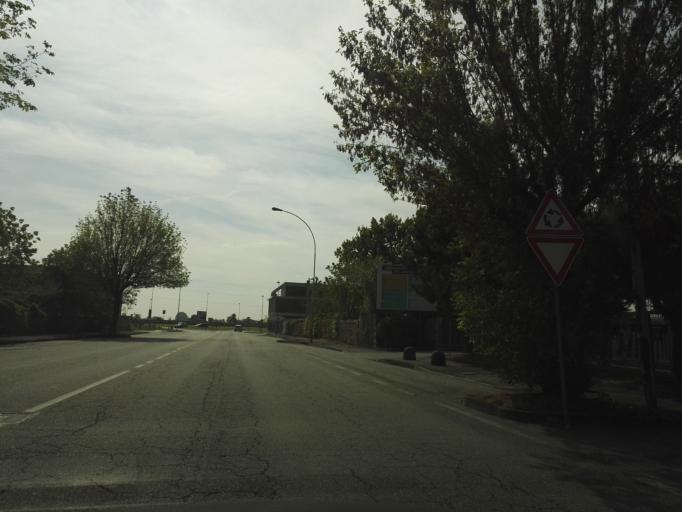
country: IT
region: Lombardy
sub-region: Citta metropolitana di Milano
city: Bettola-Zeloforomagno
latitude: 45.4302
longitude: 9.3241
